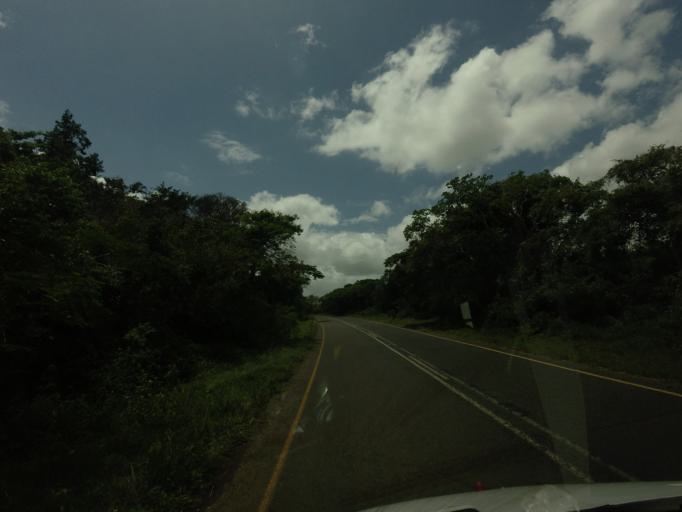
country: ZA
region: KwaZulu-Natal
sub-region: uMkhanyakude District Municipality
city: Mtubatuba
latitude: -28.3890
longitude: 32.3362
